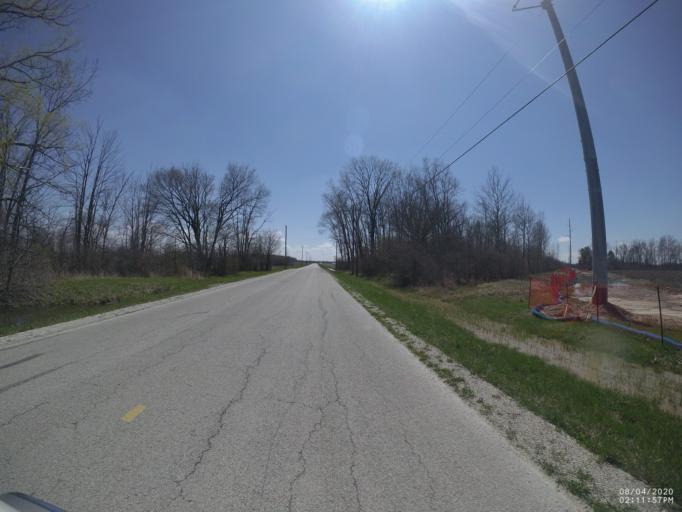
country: US
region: Ohio
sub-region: Sandusky County
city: Gibsonburg
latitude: 41.2579
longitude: -83.2645
